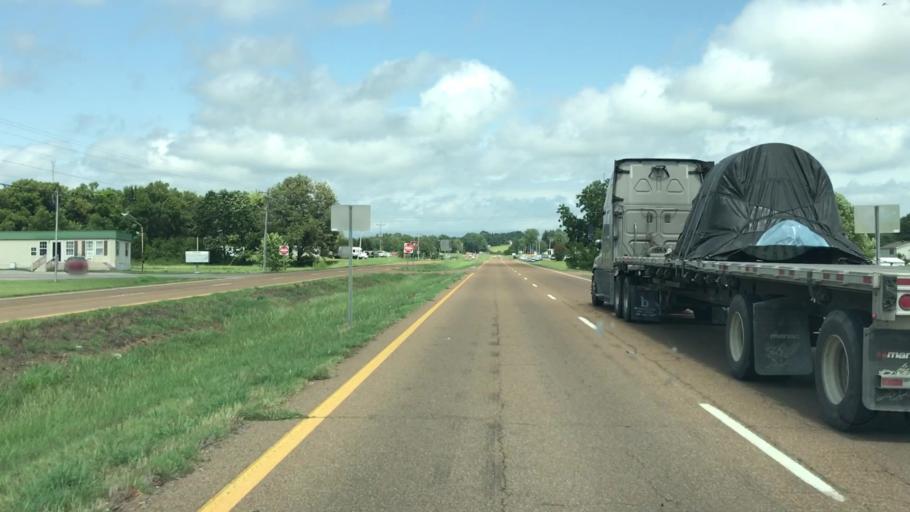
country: US
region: Tennessee
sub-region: Obion County
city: Troy
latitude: 36.3486
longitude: -89.1471
